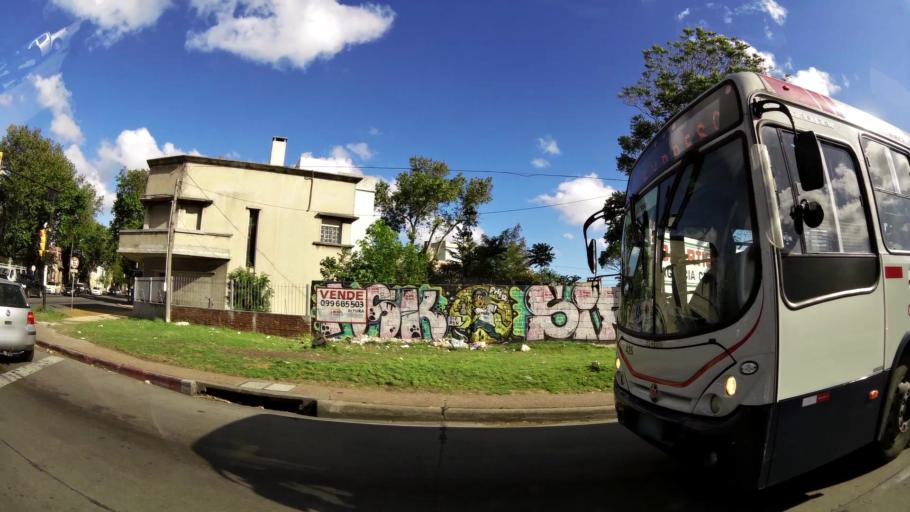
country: UY
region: Montevideo
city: Montevideo
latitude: -34.8732
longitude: -56.2055
